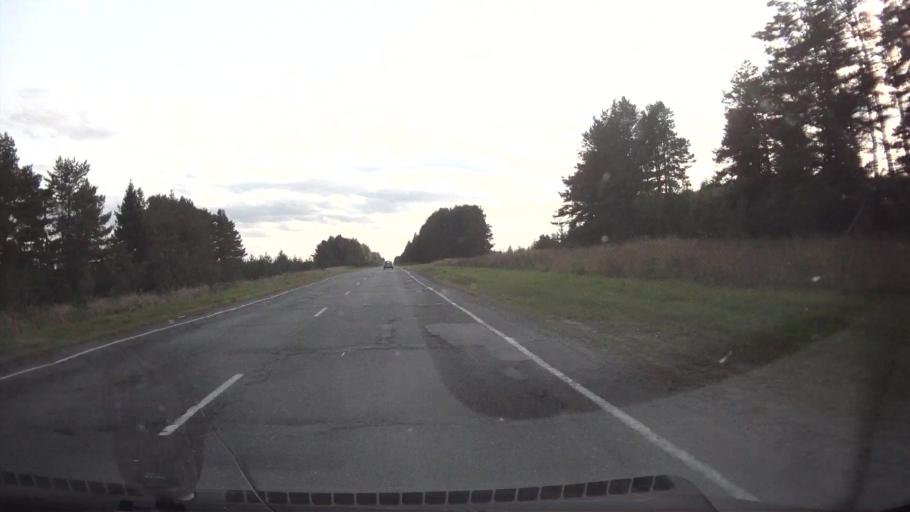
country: RU
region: Mariy-El
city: Kuzhener
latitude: 56.8408
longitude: 48.7379
